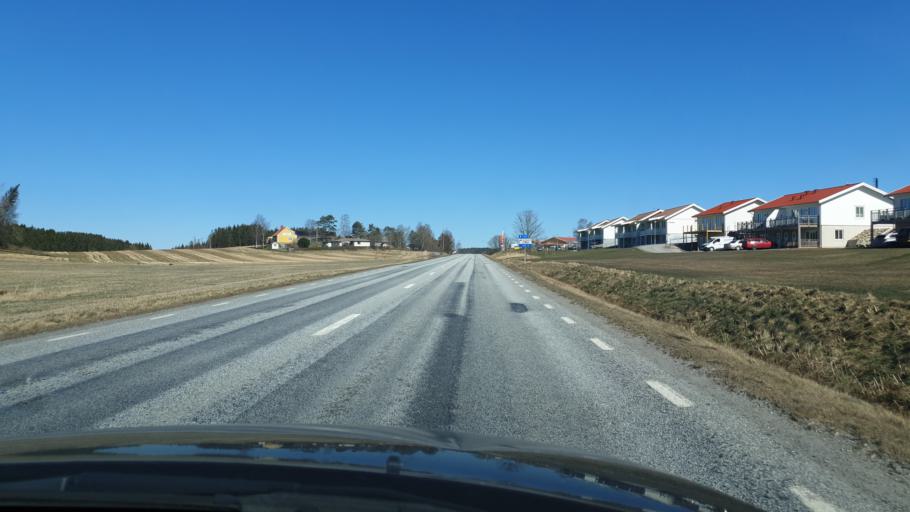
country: SE
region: Vaestra Goetaland
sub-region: Tanums Kommun
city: Tanumshede
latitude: 58.7733
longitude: 11.5581
